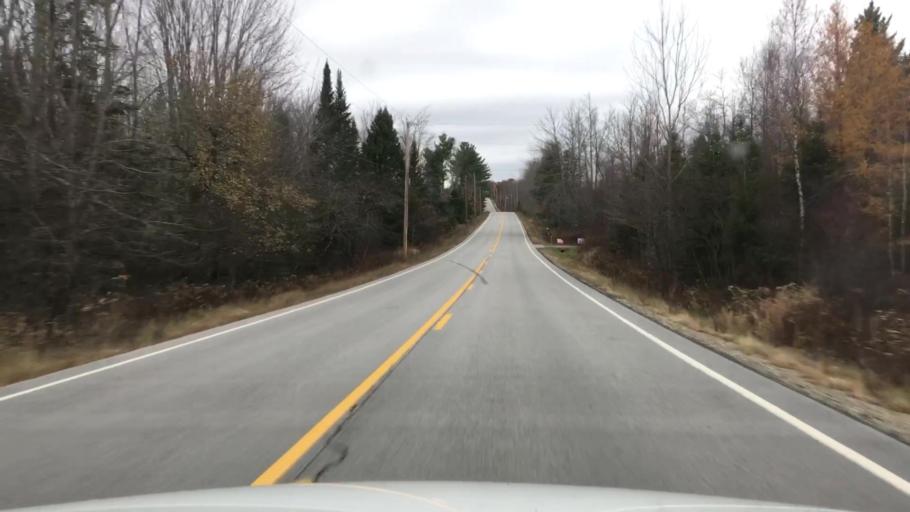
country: US
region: Maine
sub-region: Hancock County
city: Penobscot
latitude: 44.5123
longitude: -68.6573
